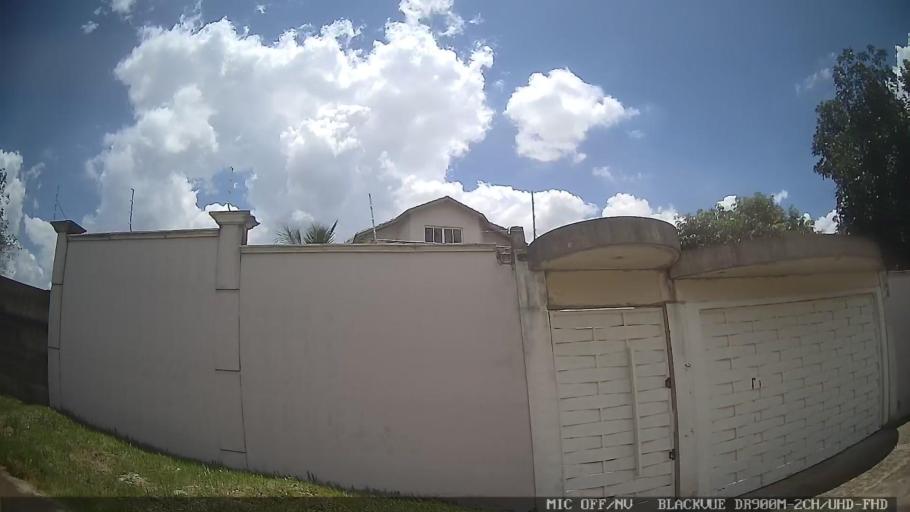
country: BR
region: Sao Paulo
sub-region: Atibaia
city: Atibaia
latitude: -23.1125
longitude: -46.5964
